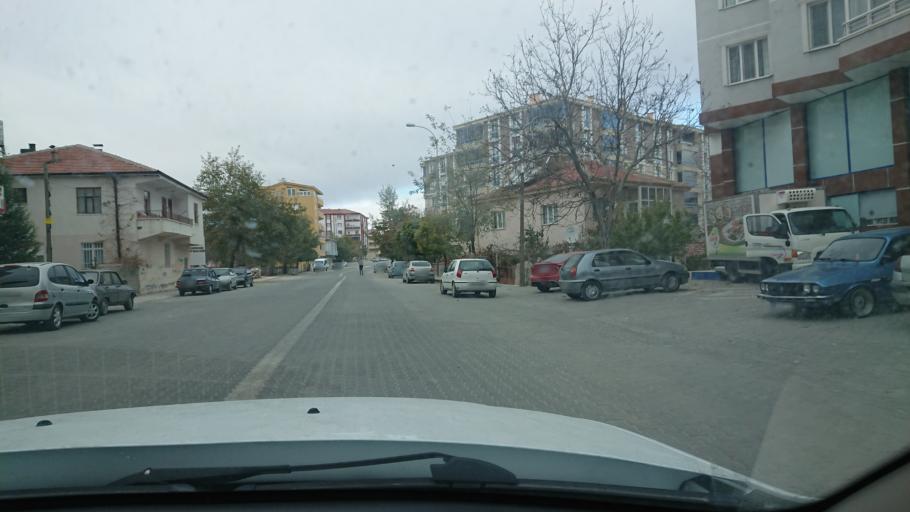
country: TR
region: Aksaray
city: Ortakoy
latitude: 38.7392
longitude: 34.0382
